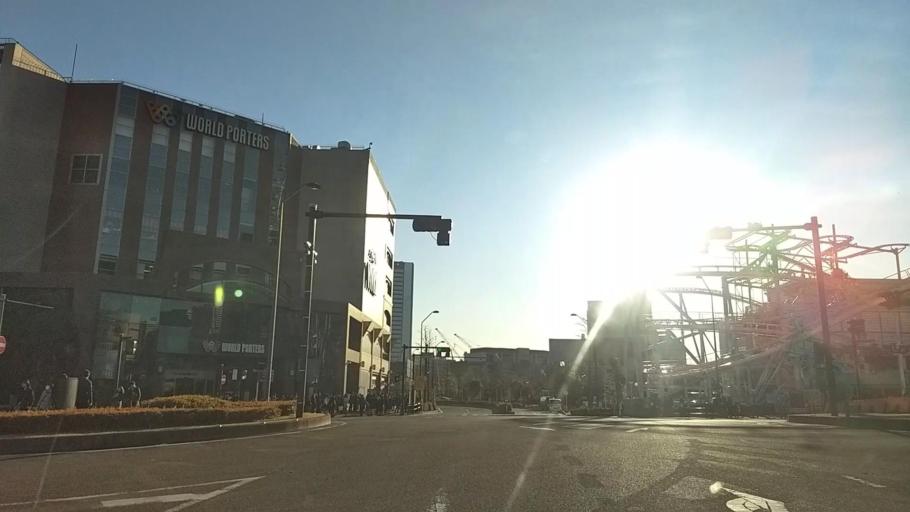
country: JP
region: Kanagawa
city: Yokohama
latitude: 35.4554
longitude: 139.6383
